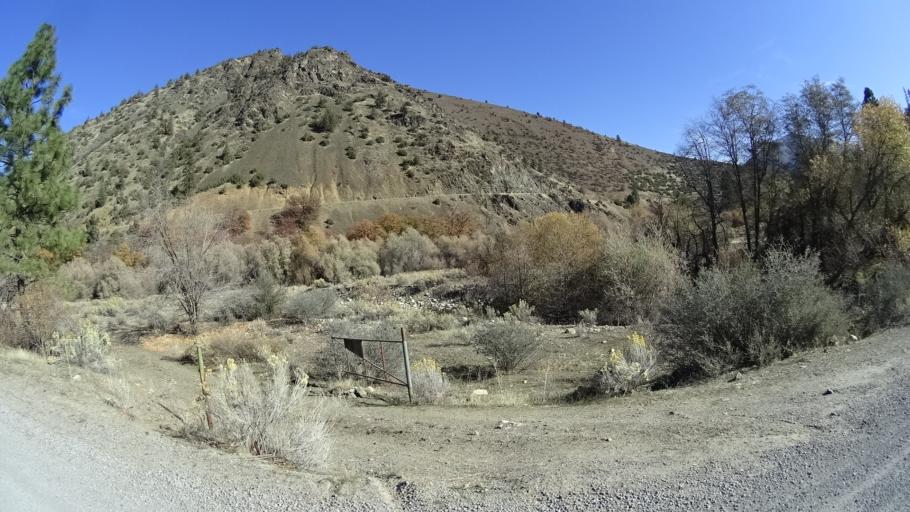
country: US
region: California
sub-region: Siskiyou County
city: Yreka
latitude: 41.8337
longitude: -122.6667
